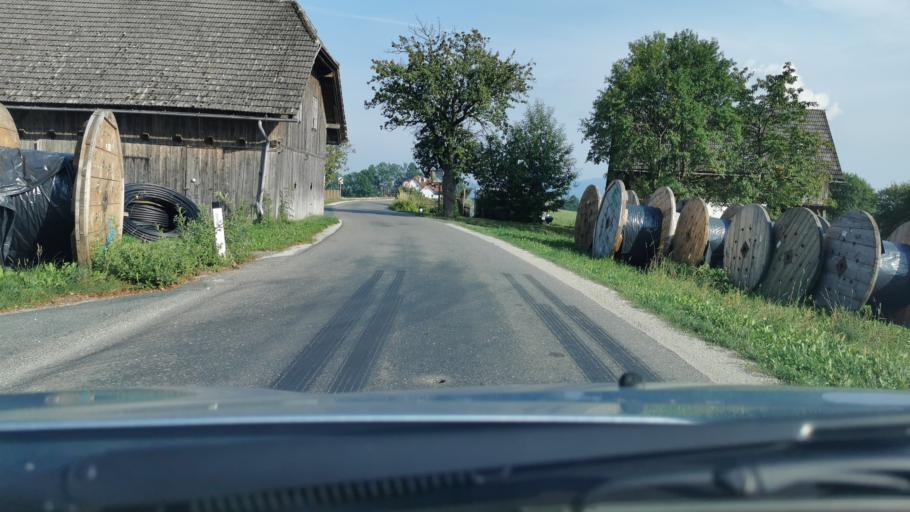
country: AT
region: Styria
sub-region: Politischer Bezirk Weiz
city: Birkfeld
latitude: 47.3762
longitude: 15.6582
